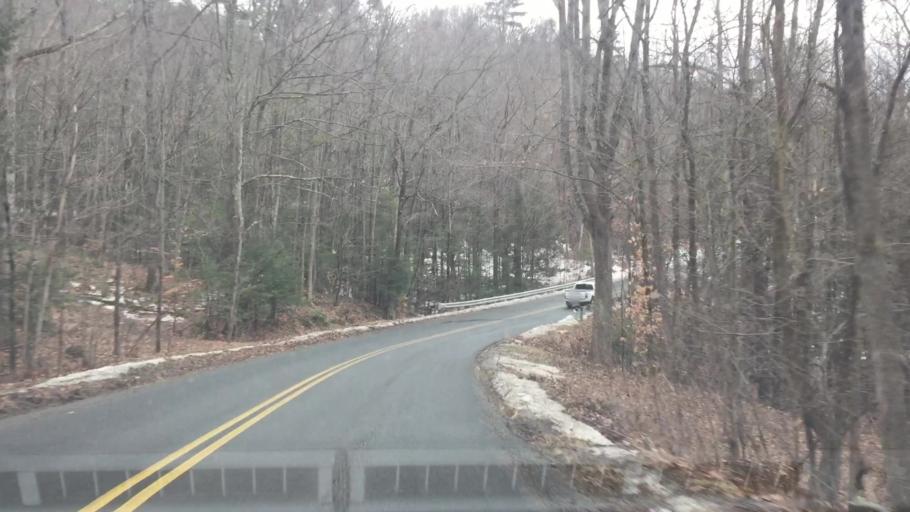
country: US
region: Massachusetts
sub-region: Hampshire County
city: Westhampton
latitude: 42.2134
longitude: -72.8487
